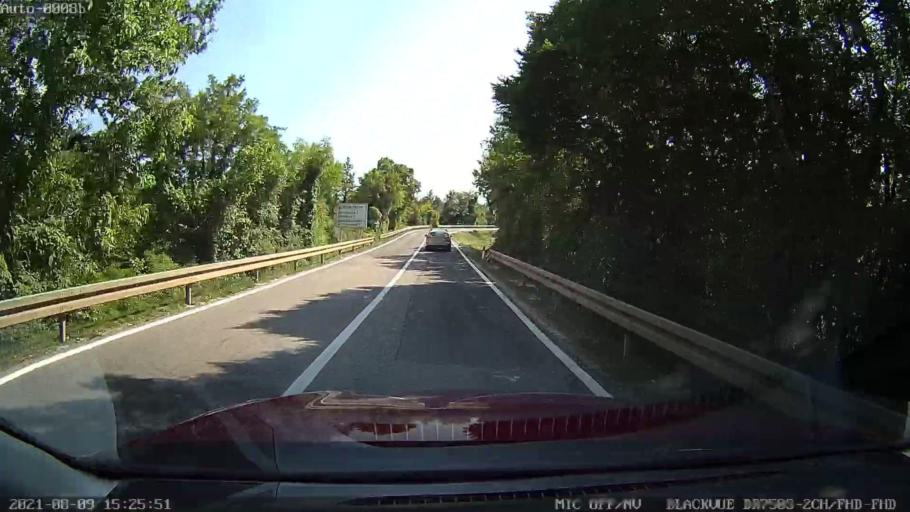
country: HR
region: Istarska
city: Pazin
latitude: 45.1663
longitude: 13.9092
